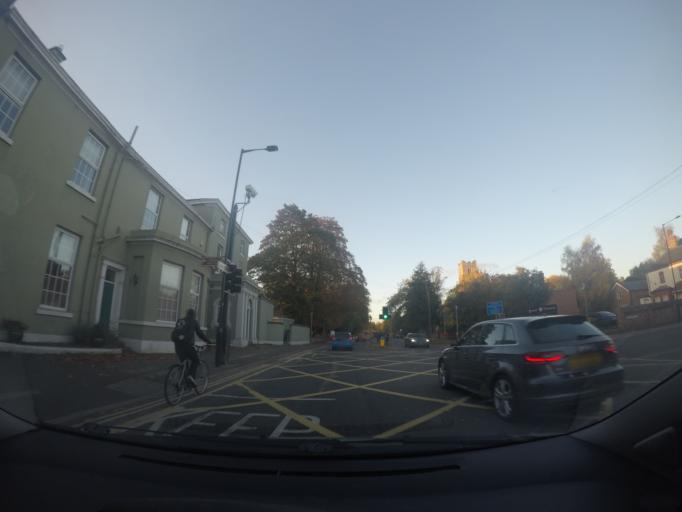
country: GB
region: England
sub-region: City of York
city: Fulford
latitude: 53.9374
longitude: -1.0734
